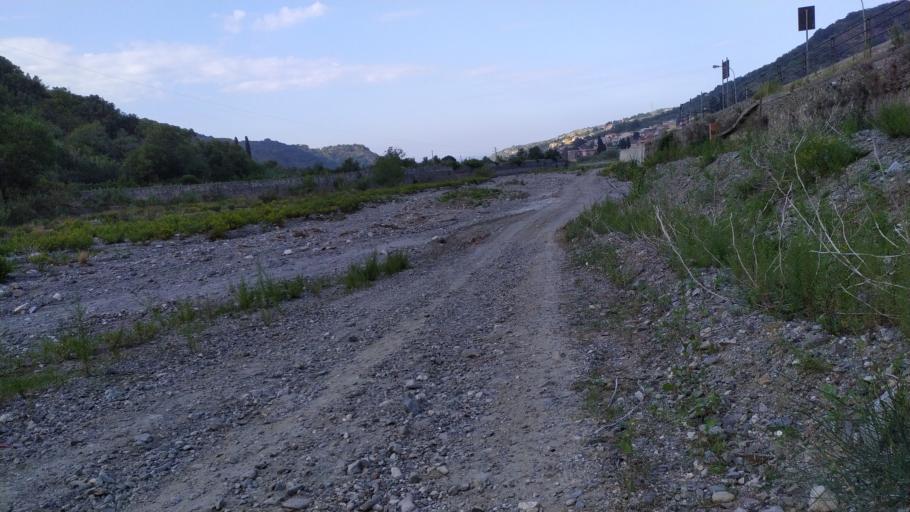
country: IT
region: Sicily
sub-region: Messina
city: Saponara
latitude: 38.1986
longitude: 15.4298
